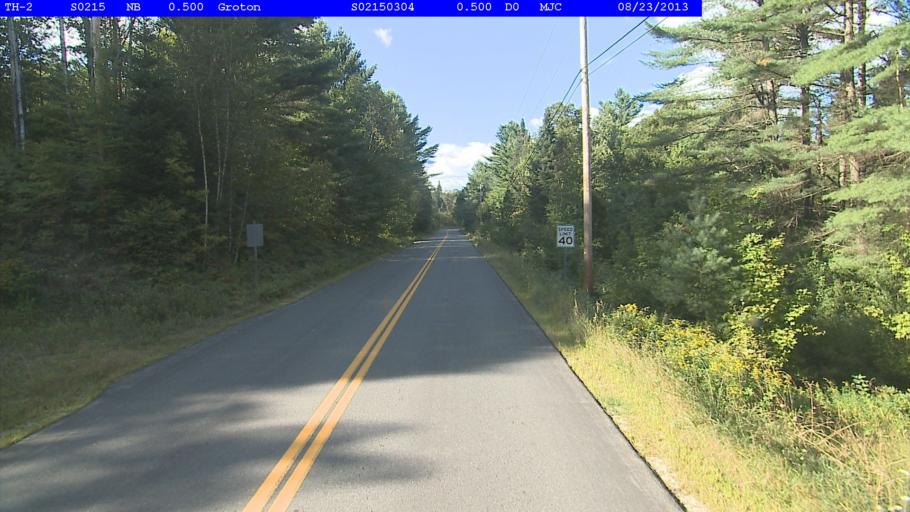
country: US
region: New Hampshire
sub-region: Grafton County
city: Woodsville
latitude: 44.2161
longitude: -72.1917
